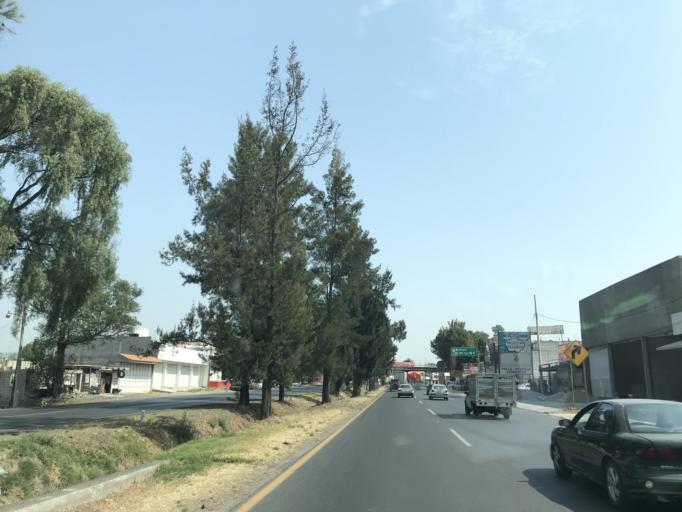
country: MX
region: Tlaxcala
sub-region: Apetatitlan de Antonio Carvajal
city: Tlatempan
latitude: 19.3271
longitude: -98.2002
